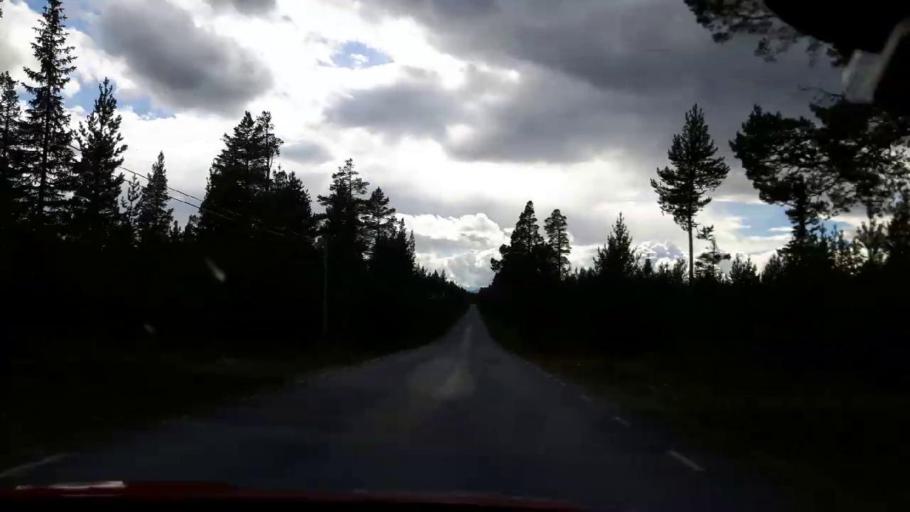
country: SE
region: Jaemtland
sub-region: Are Kommun
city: Are
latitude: 63.1738
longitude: 13.0926
